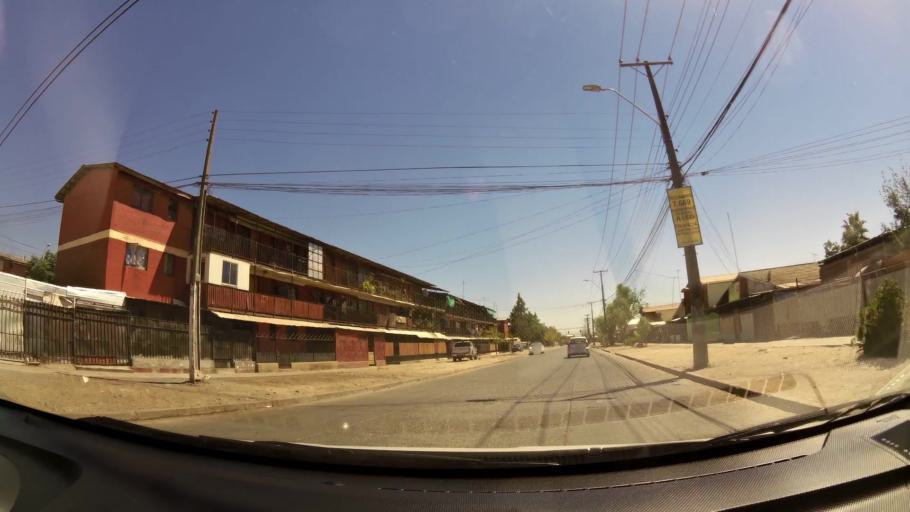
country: CL
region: O'Higgins
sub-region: Provincia de Cachapoal
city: Rancagua
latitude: -34.1651
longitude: -70.7198
